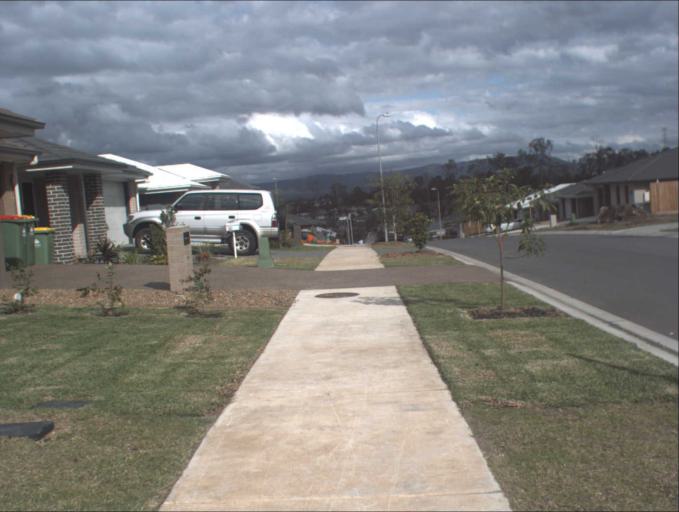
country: AU
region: Queensland
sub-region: Logan
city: Chambers Flat
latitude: -27.7983
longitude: 153.1041
